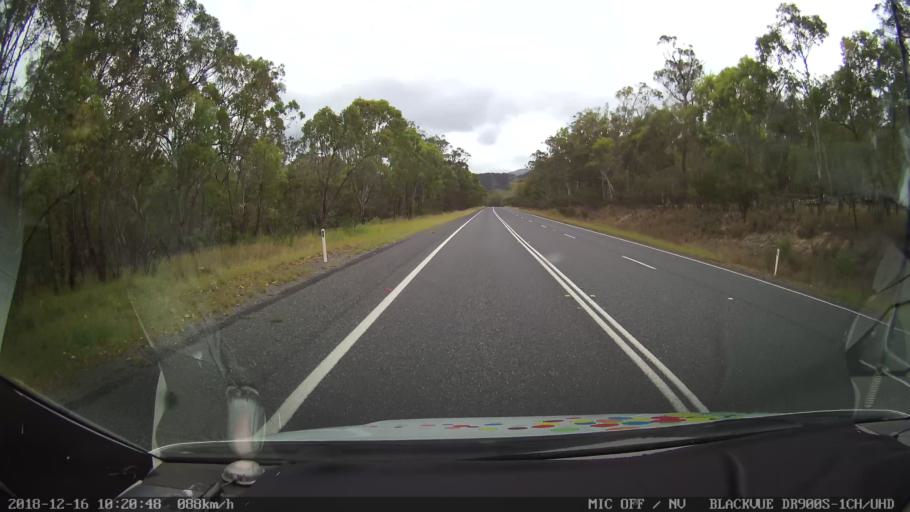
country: AU
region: New South Wales
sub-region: Tenterfield Municipality
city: Carrolls Creek
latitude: -29.2153
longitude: 152.0104
